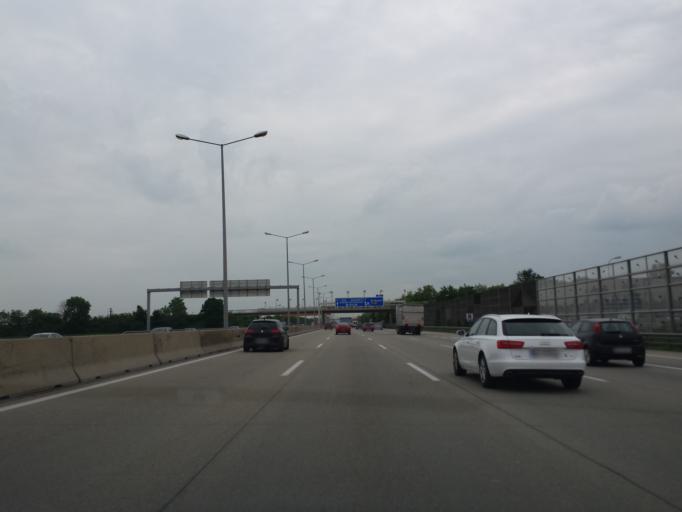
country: AT
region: Lower Austria
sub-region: Politischer Bezirk Modling
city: Wiener Neudorf
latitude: 48.0938
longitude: 16.3251
